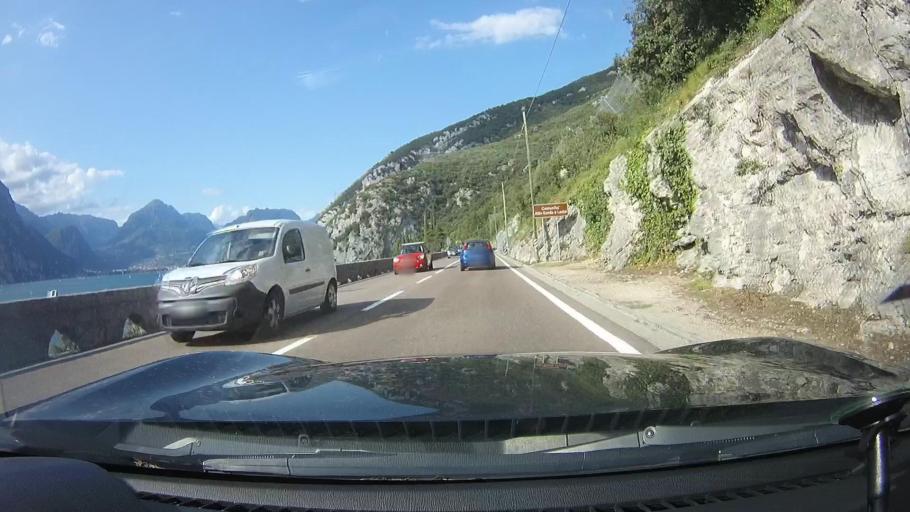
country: IT
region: Trentino-Alto Adige
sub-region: Provincia di Trento
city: Torbole sul Garda
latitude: 45.8416
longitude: 10.8619
